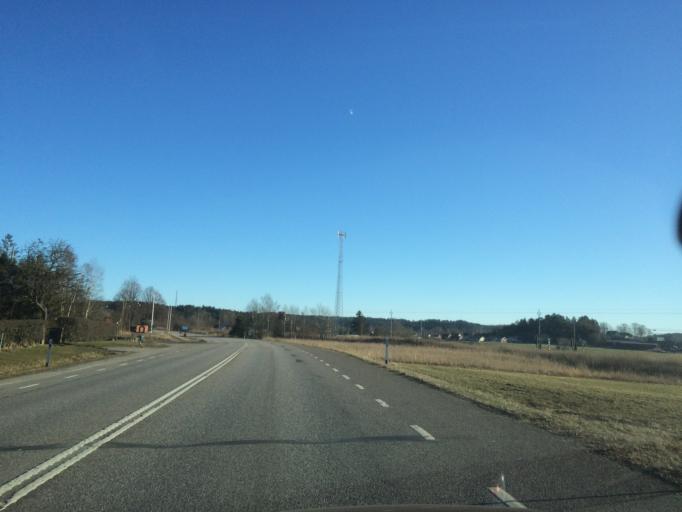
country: SE
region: Vaestra Goetaland
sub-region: Molndal
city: Lindome
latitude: 57.5328
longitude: 12.0974
